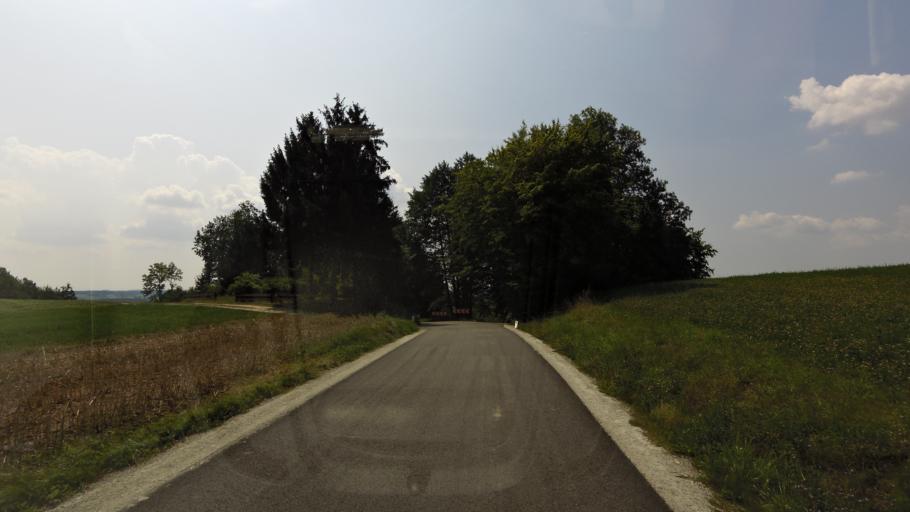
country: AT
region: Upper Austria
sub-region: Politischer Bezirk Ried im Innkreis
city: Waldzell
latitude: 48.2152
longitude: 13.3548
